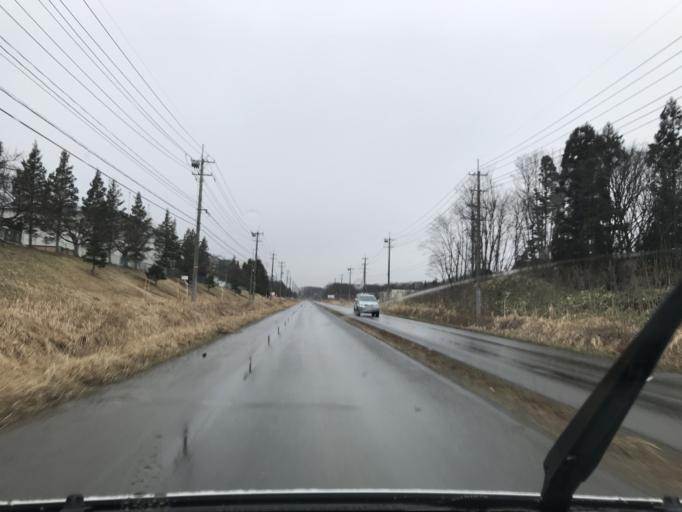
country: JP
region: Iwate
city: Kitakami
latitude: 39.2141
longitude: 141.0775
